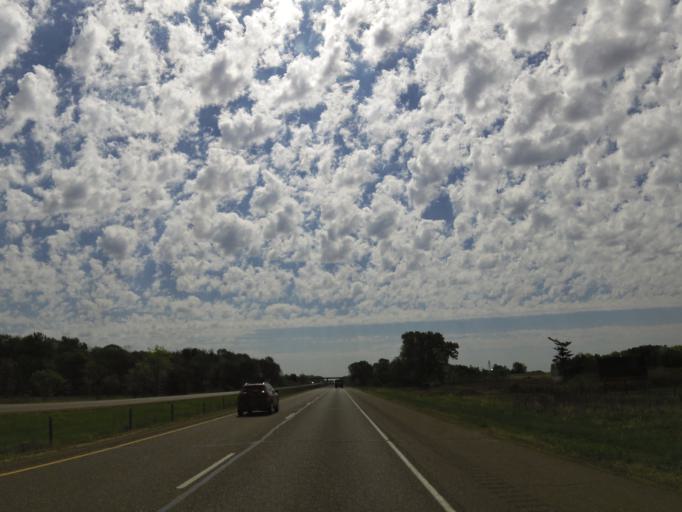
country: US
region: Wisconsin
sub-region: Dunn County
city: Colfax
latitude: 44.8755
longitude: -91.7089
